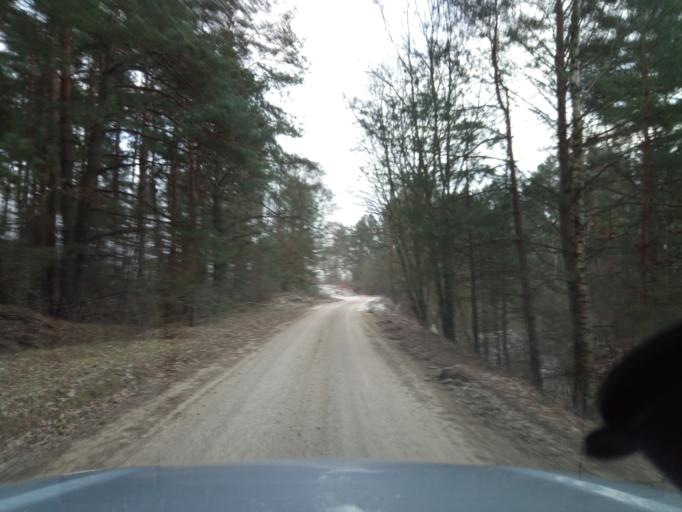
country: LT
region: Alytaus apskritis
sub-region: Alytaus rajonas
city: Daugai
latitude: 54.3177
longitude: 24.3600
